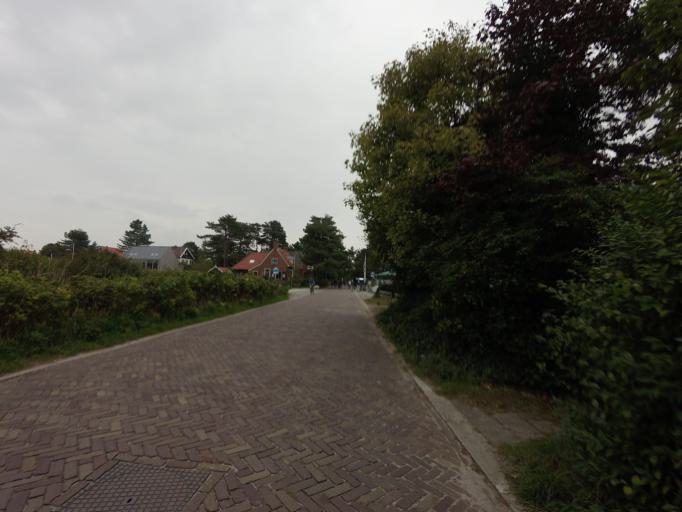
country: NL
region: Friesland
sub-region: Gemeente Schiermonnikoog
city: Schiermonnikoog
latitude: 53.4820
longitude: 6.1601
